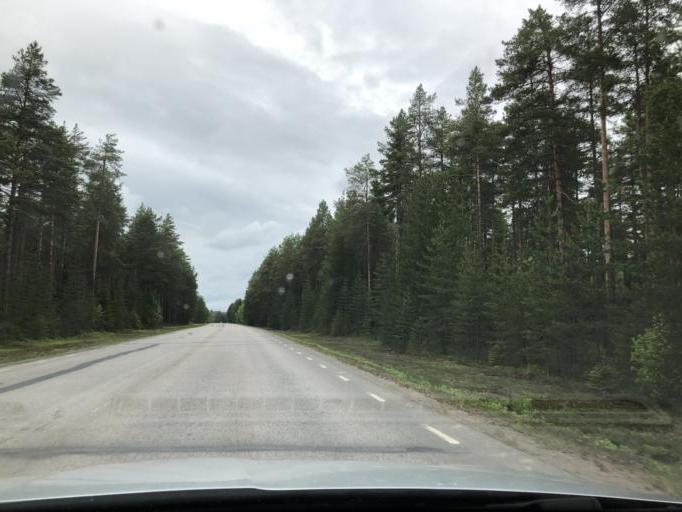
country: SE
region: Norrbotten
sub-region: Pitea Kommun
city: Bergsviken
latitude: 65.3620
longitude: 21.3714
